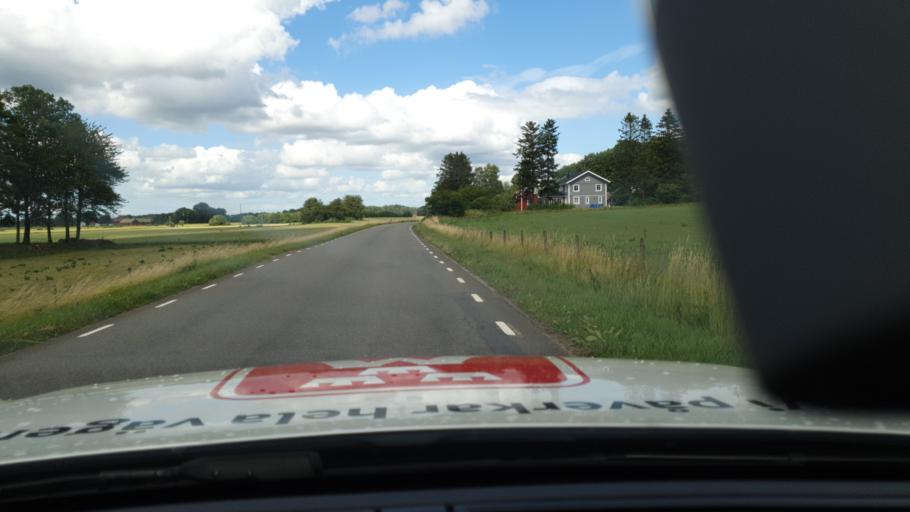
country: SE
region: Vaestra Goetaland
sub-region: Skara Kommun
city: Axvall
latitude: 58.3566
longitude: 13.6230
